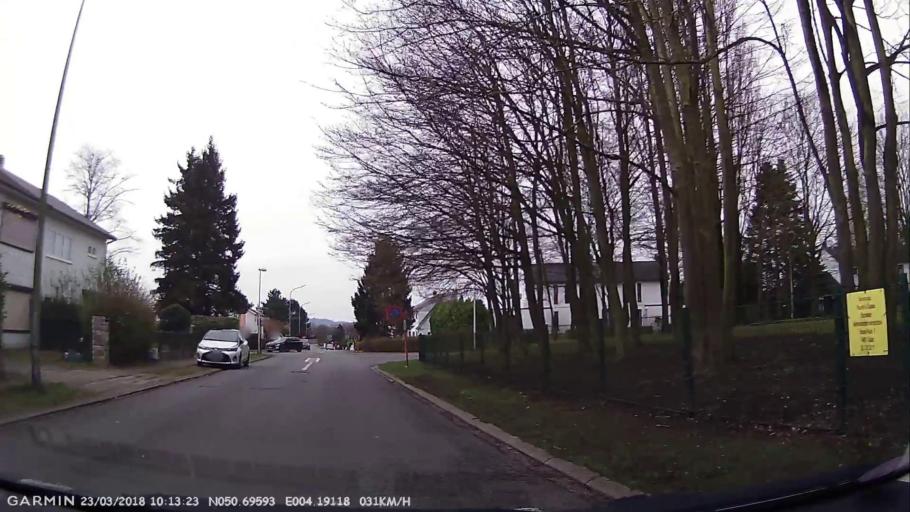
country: BE
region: Wallonia
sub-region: Province du Brabant Wallon
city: Tubize
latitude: 50.6959
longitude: 4.1911
